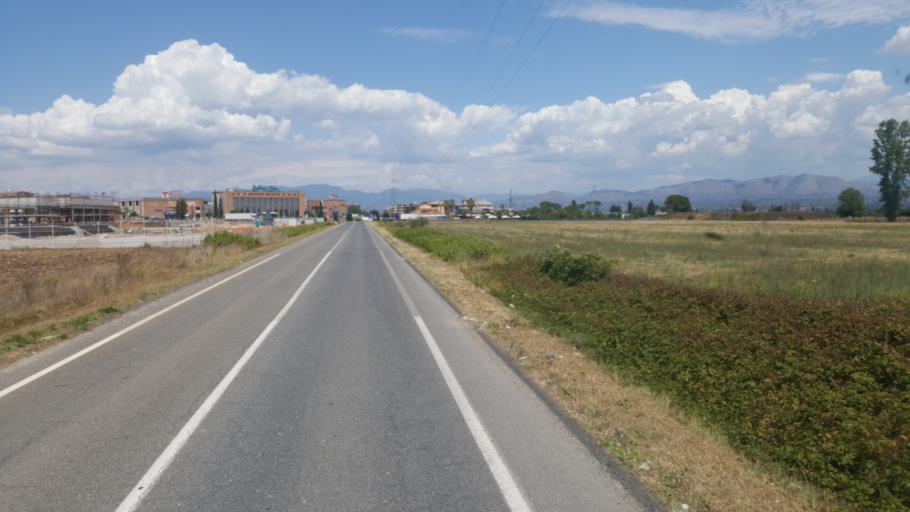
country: IT
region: Latium
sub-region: Citta metropolitana di Roma Capitale
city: Bivio di Capanelle
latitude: 42.1369
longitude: 12.5982
